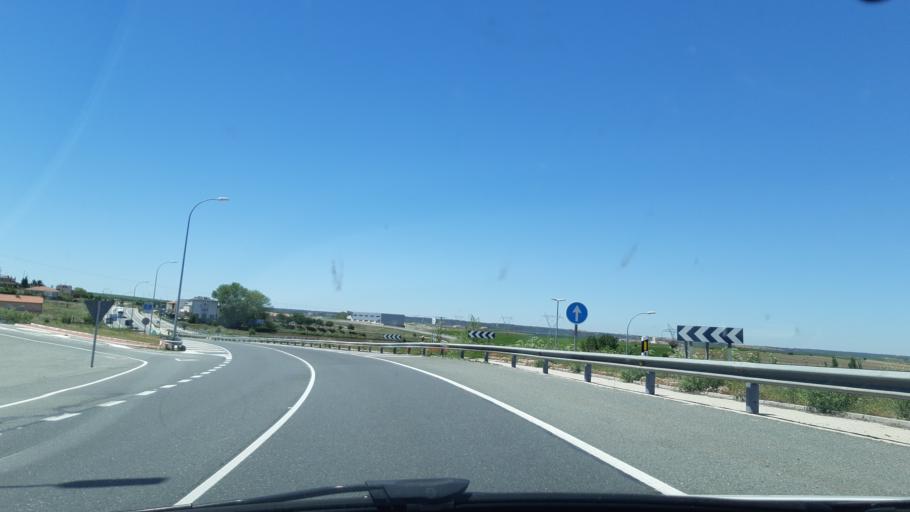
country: ES
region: Castille and Leon
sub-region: Provincia de Segovia
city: Villacastin
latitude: 40.7822
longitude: -4.4118
